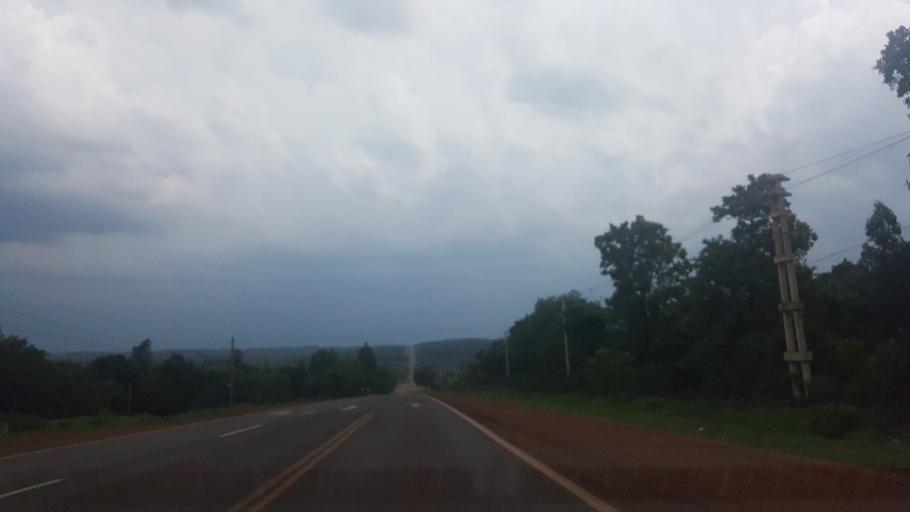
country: AR
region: Misiones
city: Santo Pipo
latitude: -27.1468
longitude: -55.4112
